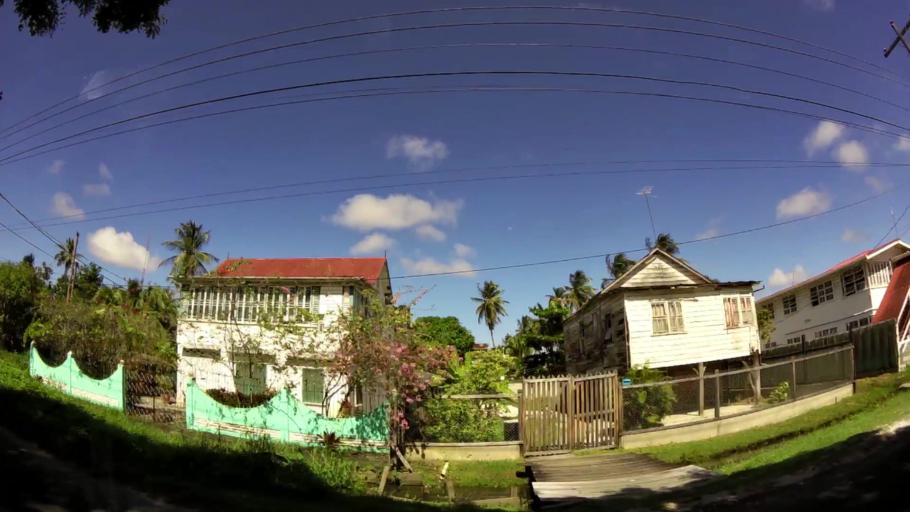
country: GY
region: Demerara-Mahaica
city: Georgetown
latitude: 6.8114
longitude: -58.1407
